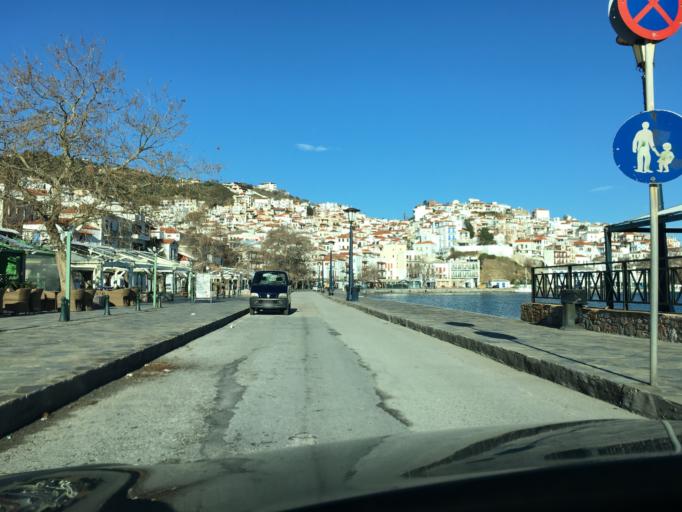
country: GR
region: Thessaly
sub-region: Nomos Magnisias
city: Skopelos
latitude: 39.1210
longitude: 23.7294
